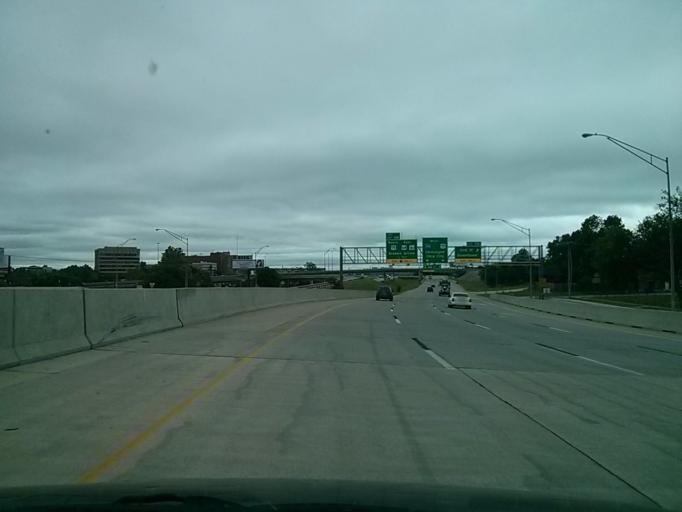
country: US
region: Oklahoma
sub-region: Tulsa County
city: Tulsa
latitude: 36.1548
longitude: -96.0014
